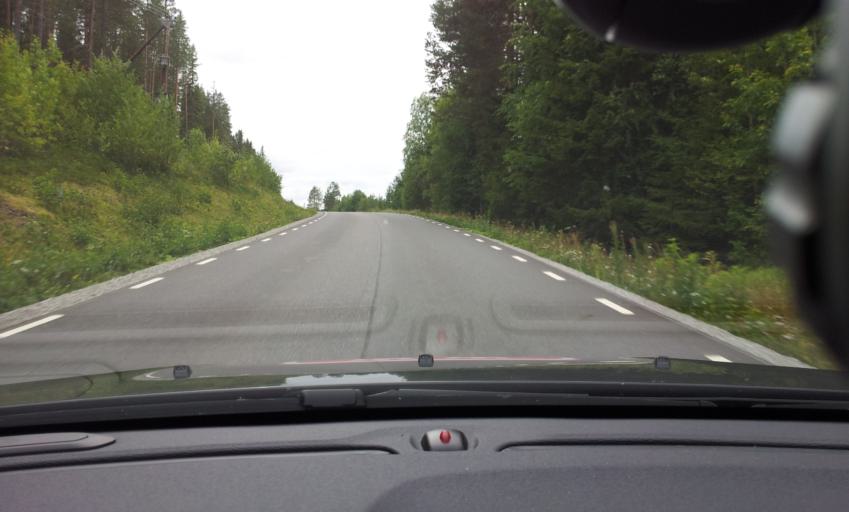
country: SE
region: Jaemtland
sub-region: Braecke Kommun
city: Braecke
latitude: 63.1363
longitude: 15.5183
